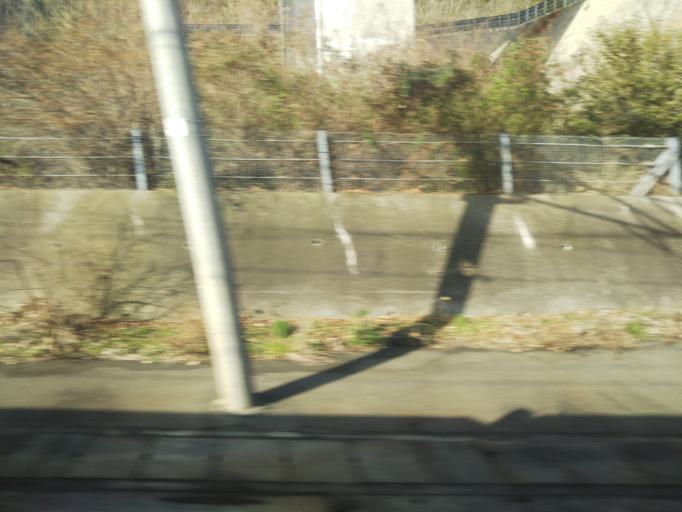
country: JP
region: Kagawa
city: Sakaidecho
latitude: 34.4455
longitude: 133.8083
